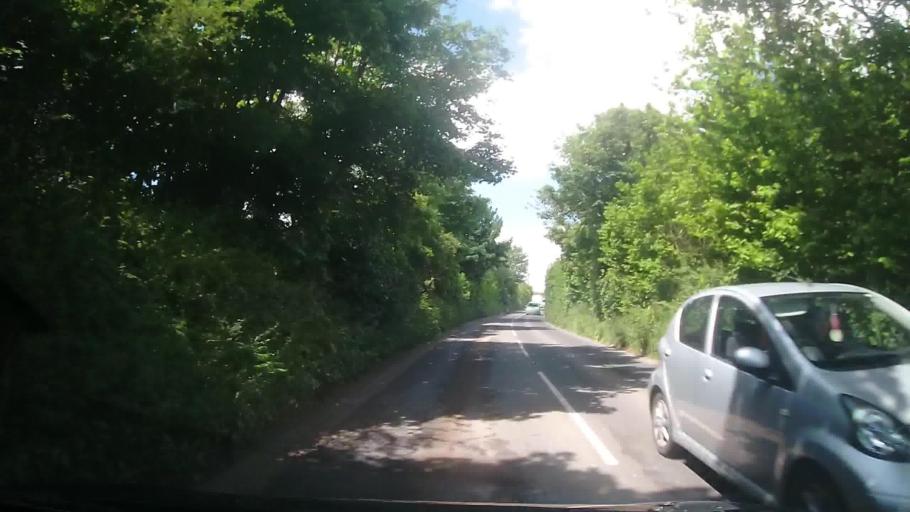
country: GB
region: England
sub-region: Devon
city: Dartmouth
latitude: 50.3469
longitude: -3.6069
